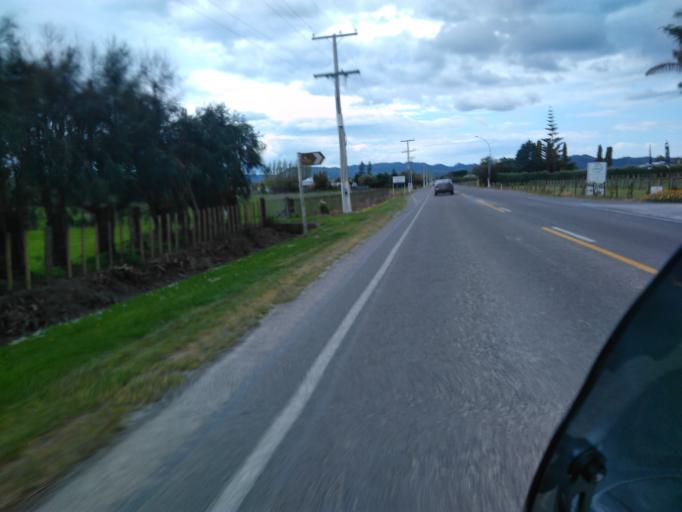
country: NZ
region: Gisborne
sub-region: Gisborne District
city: Gisborne
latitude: -38.6551
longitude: 177.9525
